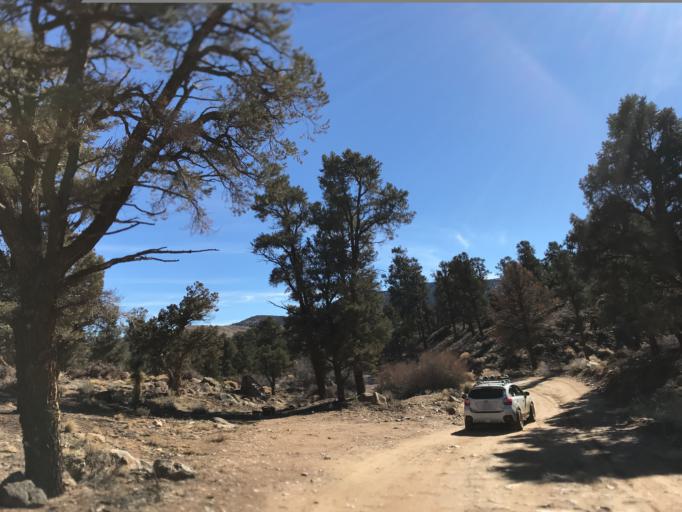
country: US
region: California
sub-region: San Bernardino County
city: Big Bear City
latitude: 34.2621
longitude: -116.7538
